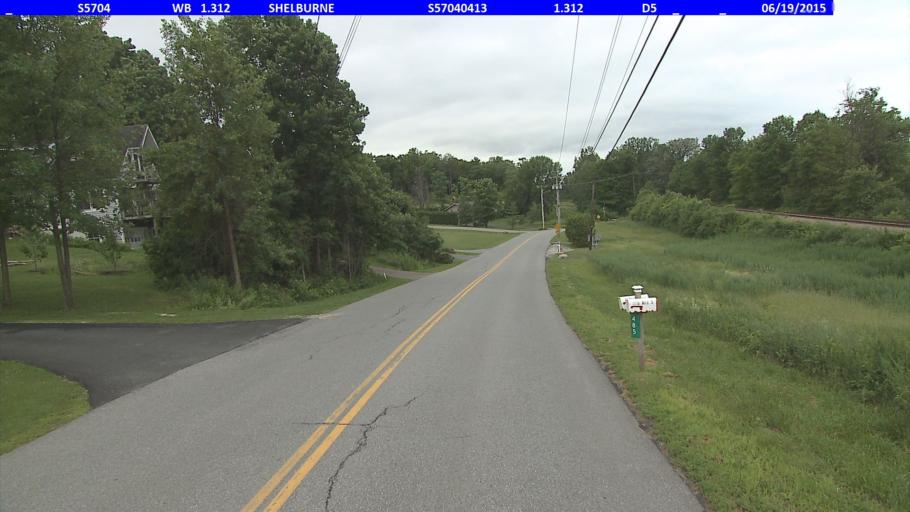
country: US
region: Vermont
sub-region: Chittenden County
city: Burlington
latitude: 44.4016
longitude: -73.2233
